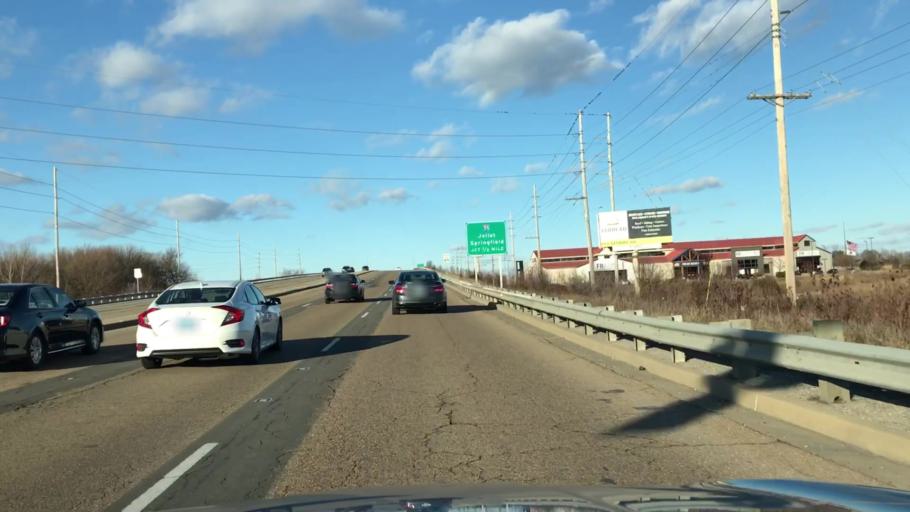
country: US
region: Illinois
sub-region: McLean County
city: Normal
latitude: 40.5251
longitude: -88.9520
